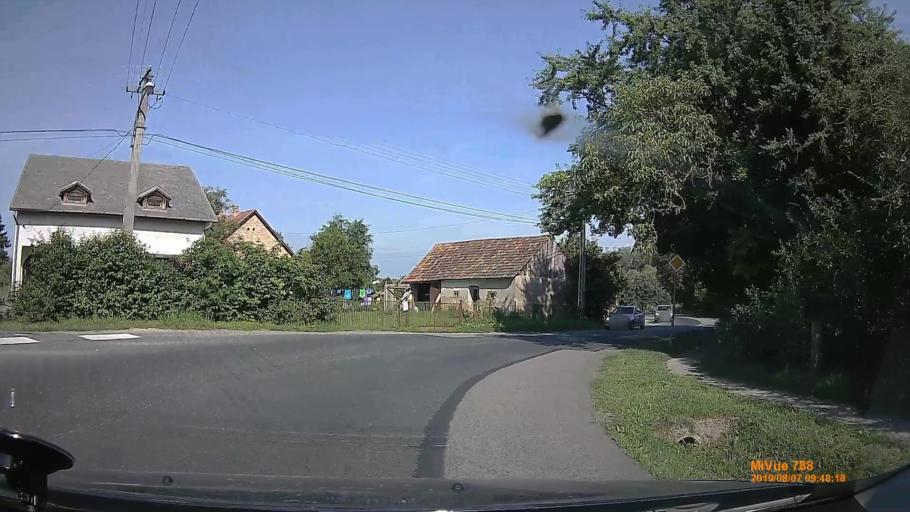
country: HU
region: Zala
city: Pacsa
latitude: 46.7288
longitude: 16.9459
